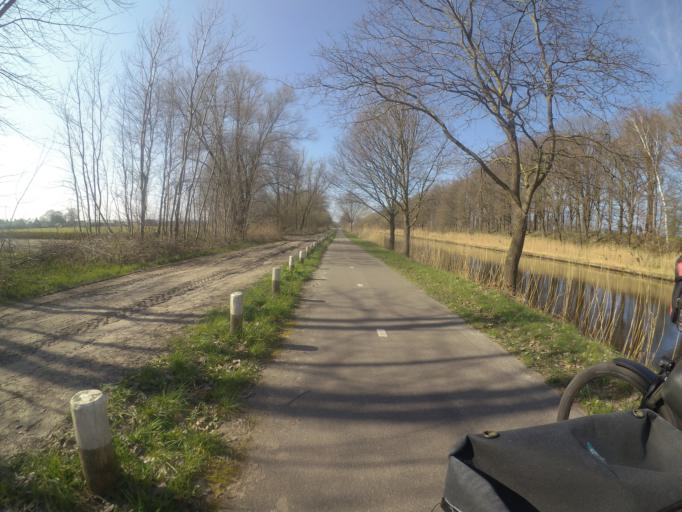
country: NL
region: North Brabant
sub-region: Gemeente Hilvarenbeek
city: Hilvarenbeek
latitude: 51.5127
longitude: 5.1585
